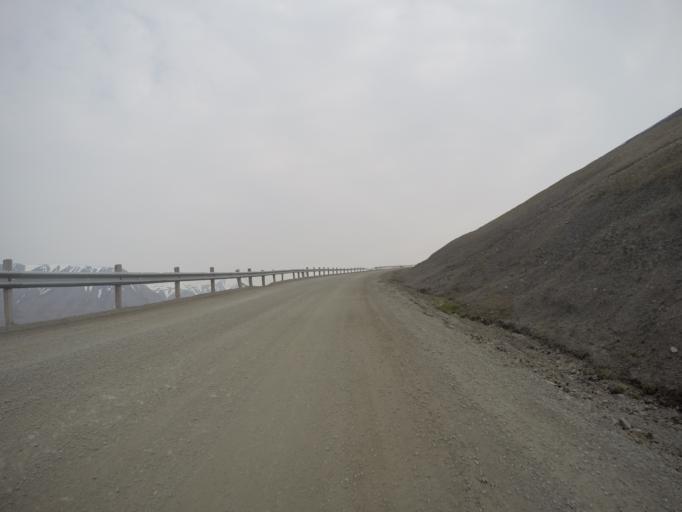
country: SJ
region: Svalbard
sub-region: Spitsbergen
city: Longyearbyen
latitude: 78.1613
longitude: 16.0235
